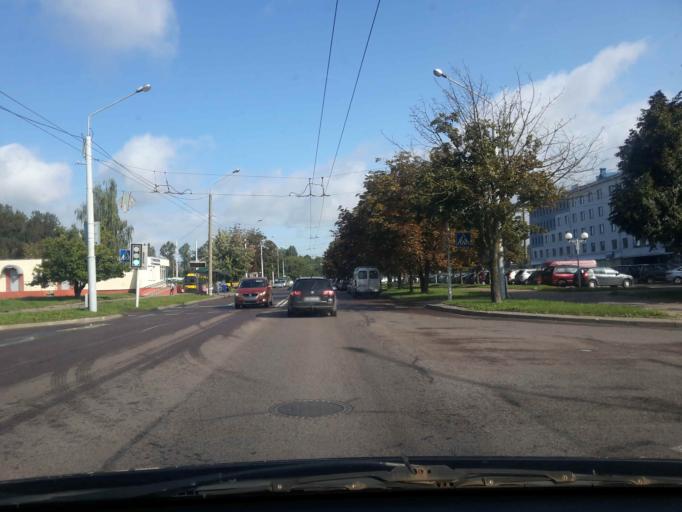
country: BY
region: Minsk
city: Minsk
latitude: 53.9395
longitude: 27.5660
